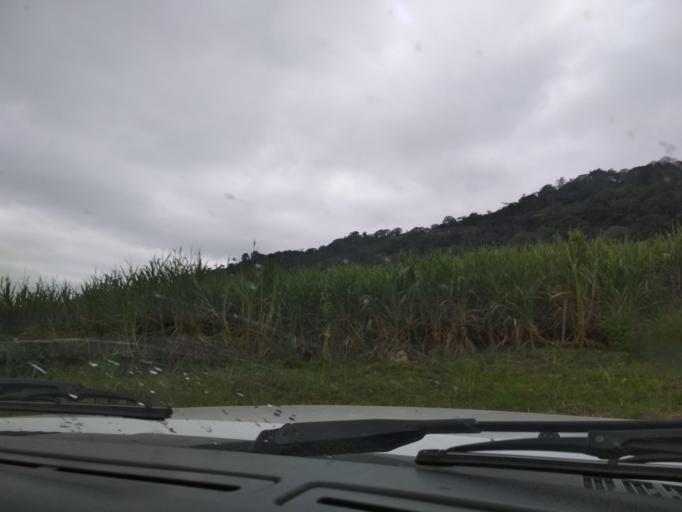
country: MX
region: Veracruz
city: El Castillo
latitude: 19.5700
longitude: -96.8496
